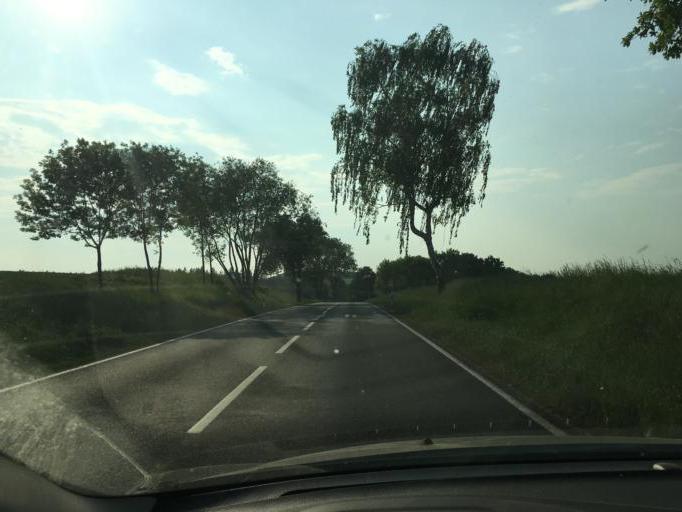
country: DE
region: Saxony
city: Colditz
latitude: 51.1400
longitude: 12.7835
